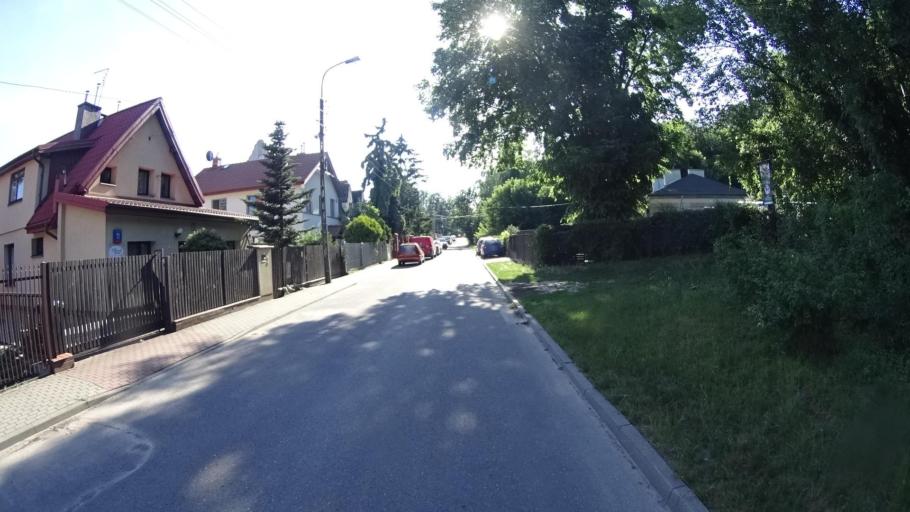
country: PL
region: Masovian Voivodeship
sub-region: Warszawa
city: Bemowo
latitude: 52.2486
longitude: 20.9461
